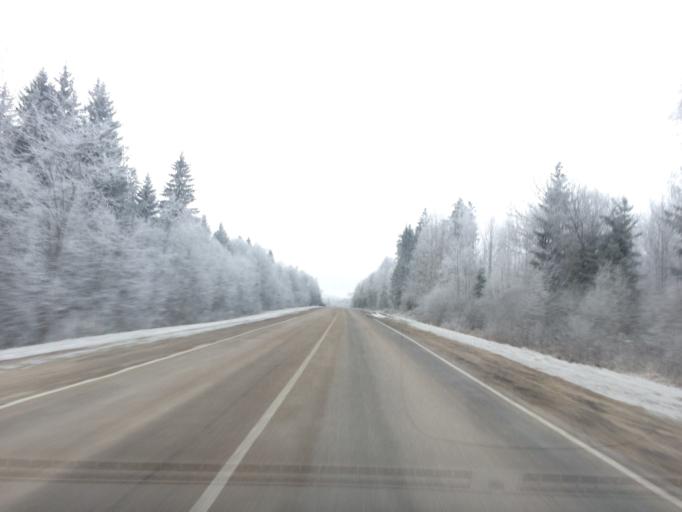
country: LV
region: Rezekne
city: Rezekne
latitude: 56.5985
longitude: 27.4217
